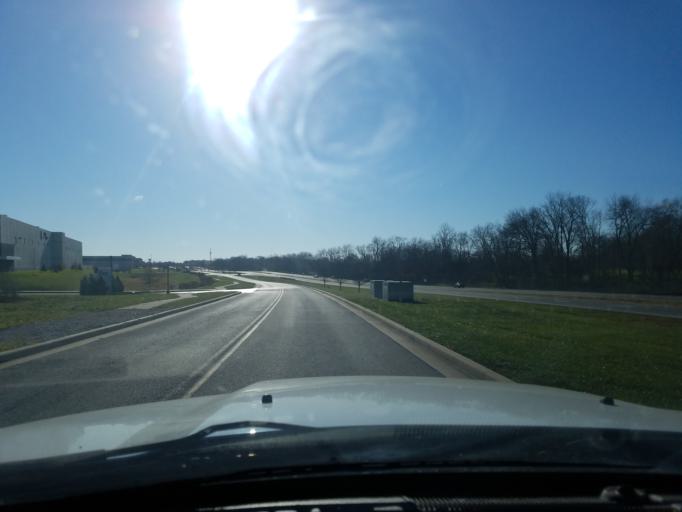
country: US
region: Indiana
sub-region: Clark County
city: Sellersburg
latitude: 38.3819
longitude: -85.6889
